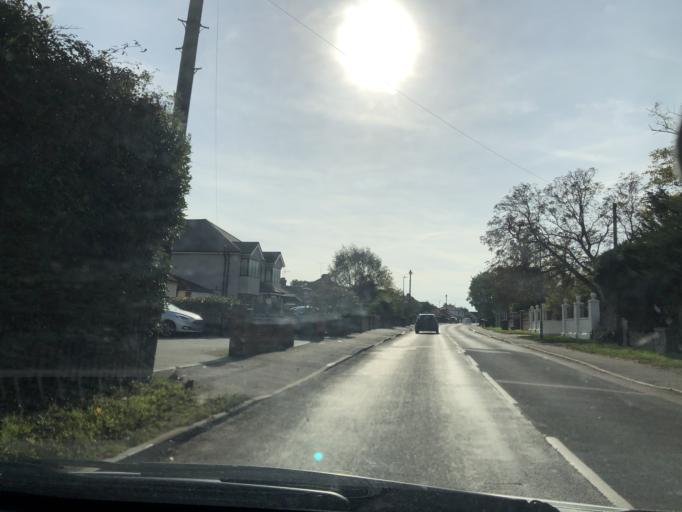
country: GB
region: England
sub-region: Kent
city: Swanley
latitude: 51.4278
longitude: 0.1806
